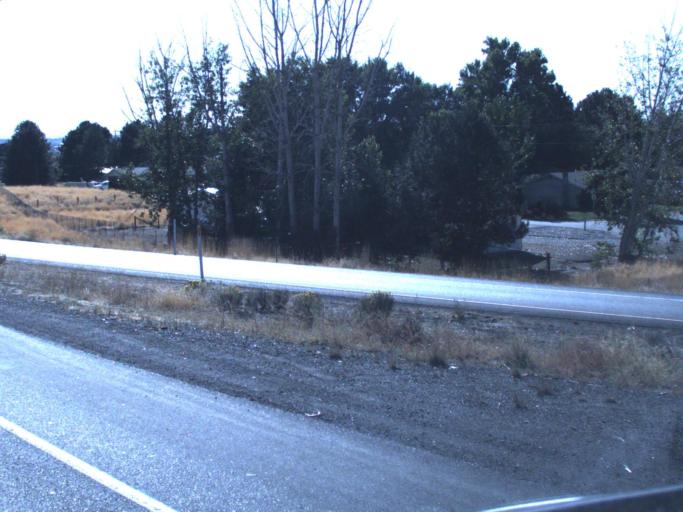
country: US
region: Washington
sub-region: Franklin County
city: Pasco
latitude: 46.2470
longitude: -119.1266
